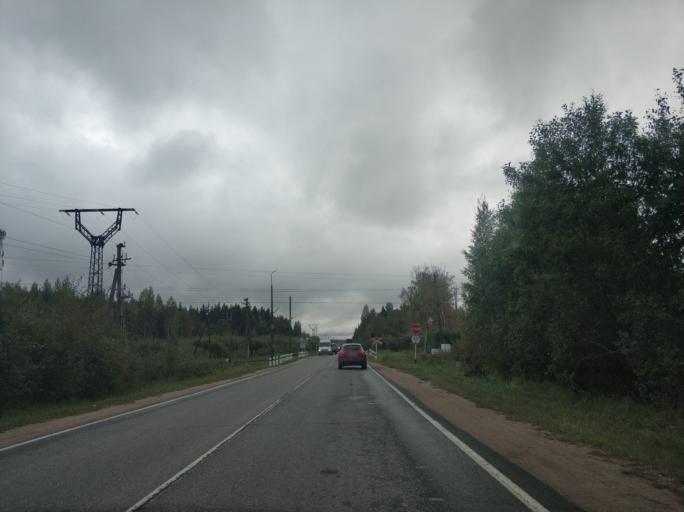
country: RU
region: Leningrad
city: Borisova Griva
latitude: 60.0958
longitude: 30.9531
